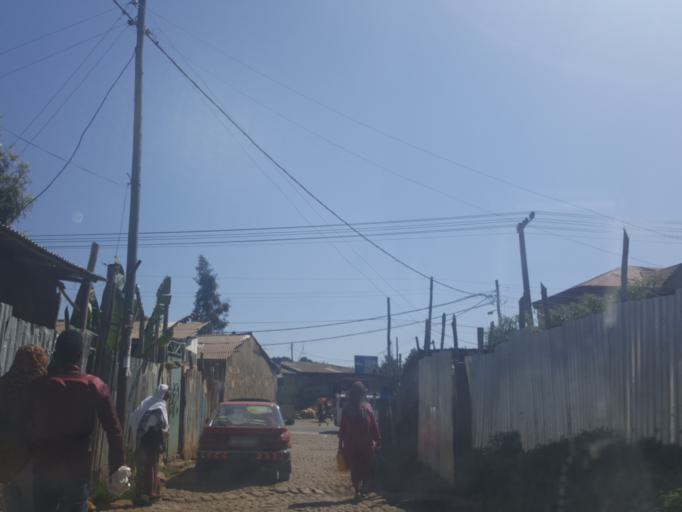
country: ET
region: Adis Abeba
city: Addis Ababa
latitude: 9.0608
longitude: 38.7273
